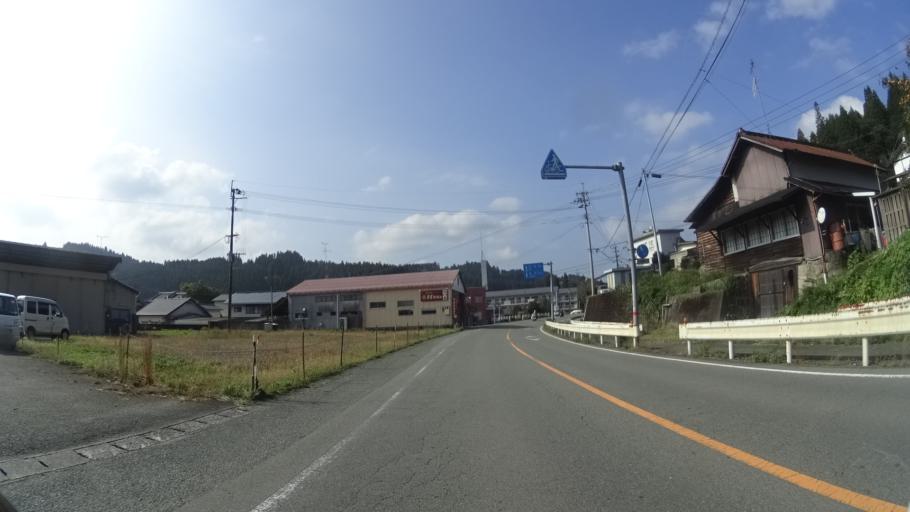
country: JP
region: Kumamoto
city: Aso
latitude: 33.1080
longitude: 131.0646
